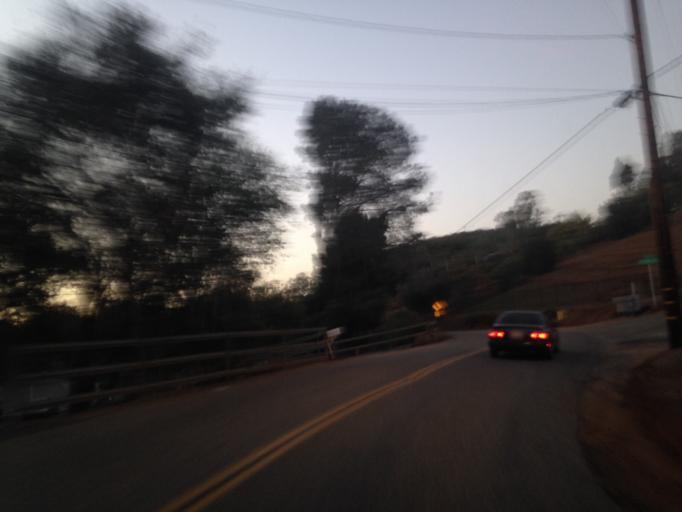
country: US
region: California
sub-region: San Diego County
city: Bonsall
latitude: 33.2612
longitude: -117.2176
